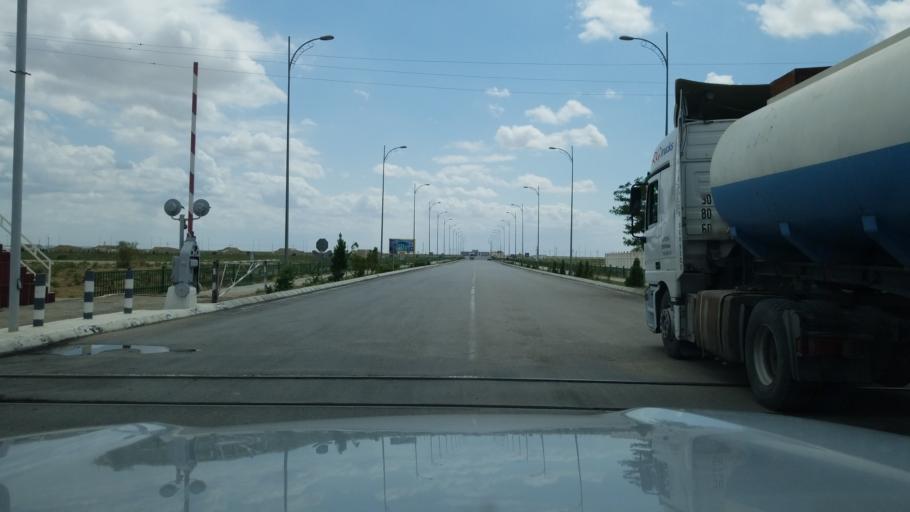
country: TM
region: Balkan
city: Balkanabat
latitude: 39.4903
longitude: 54.3772
